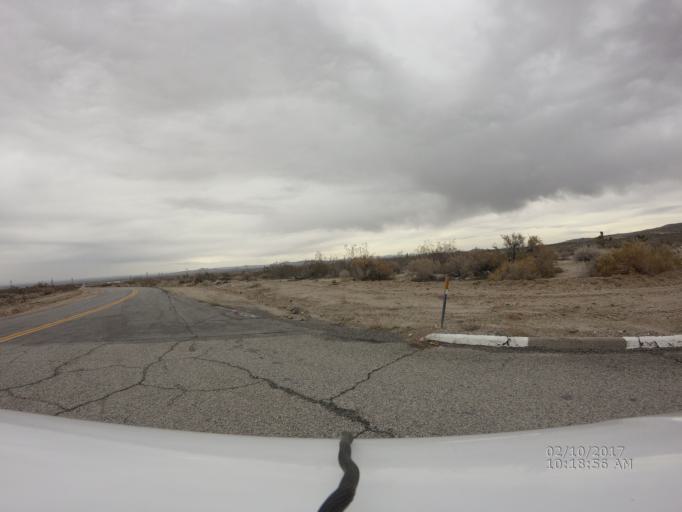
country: US
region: California
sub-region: Los Angeles County
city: Littlerock
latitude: 34.5007
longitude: -117.9580
